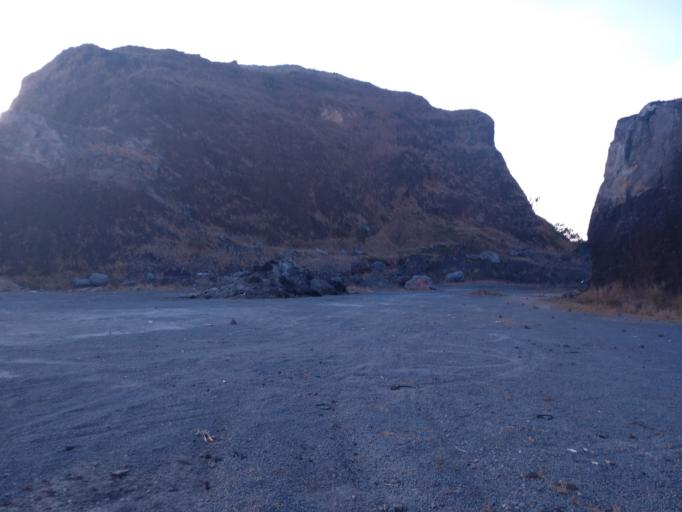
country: MX
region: Nayarit
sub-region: Tepic
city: La Corregidora
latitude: 21.4761
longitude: -104.8120
